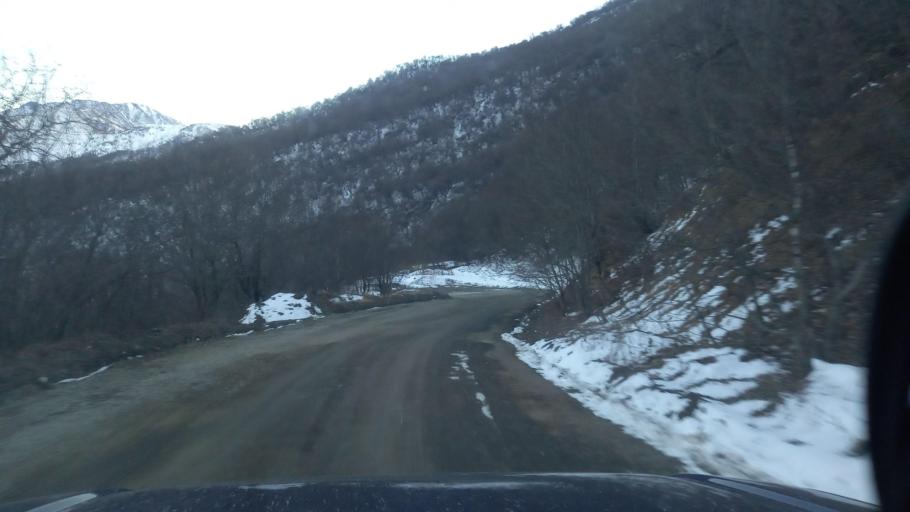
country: RU
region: Ingushetiya
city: Dzhayrakh
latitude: 42.8273
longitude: 44.5749
